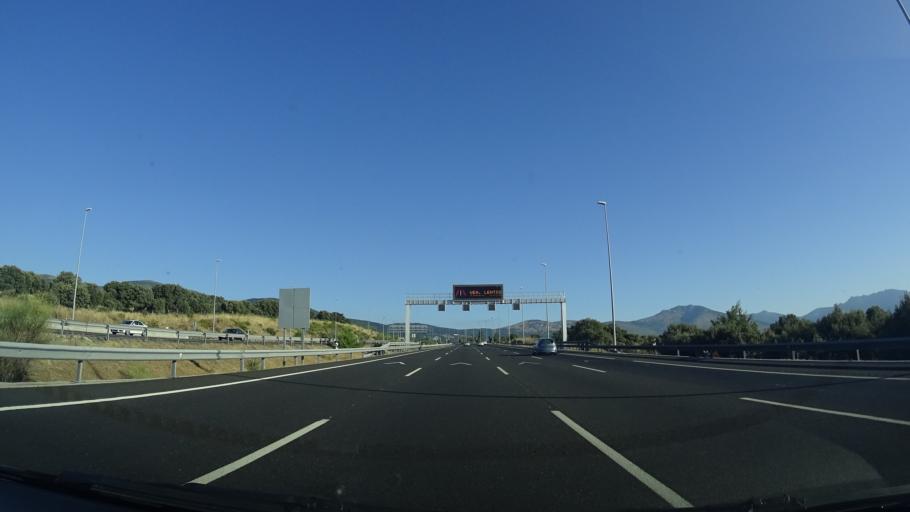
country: ES
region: Madrid
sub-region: Provincia de Madrid
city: Guadarrama
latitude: 40.6626
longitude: -4.0993
